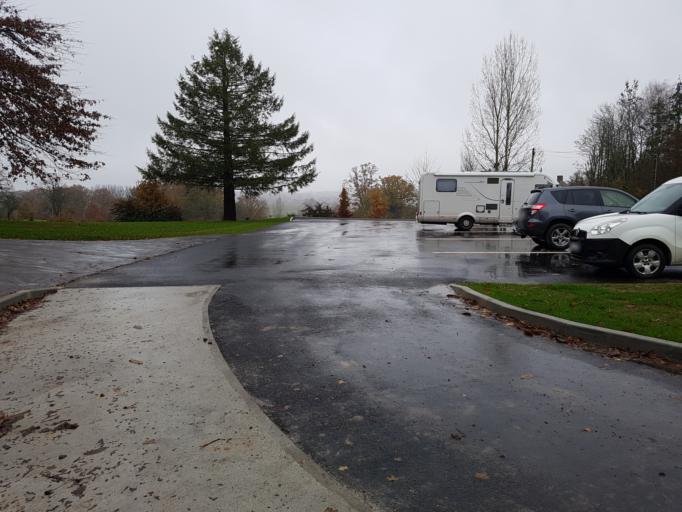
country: FR
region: Pays de la Loire
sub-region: Departement de la Mayenne
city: La Baconniere
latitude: 48.1847
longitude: -0.8917
